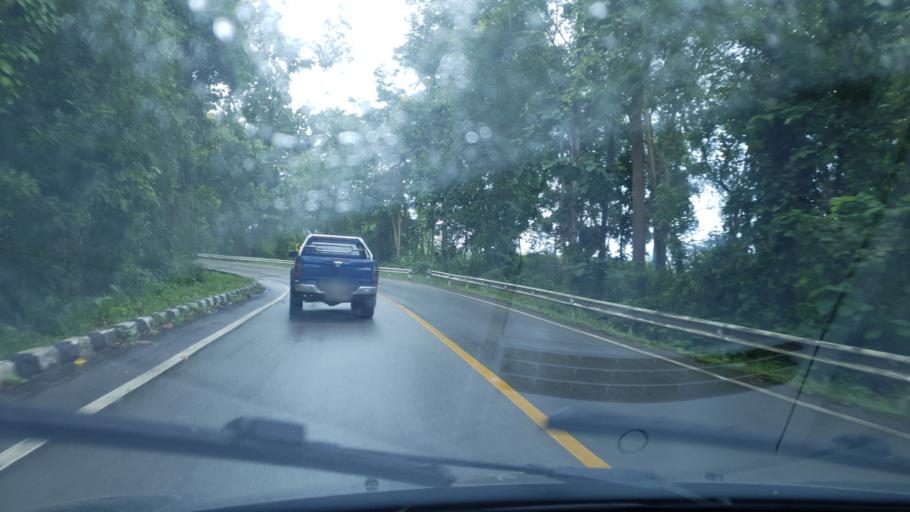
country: TH
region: Mae Hong Son
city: Mae La Noi
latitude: 18.2911
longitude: 97.9212
